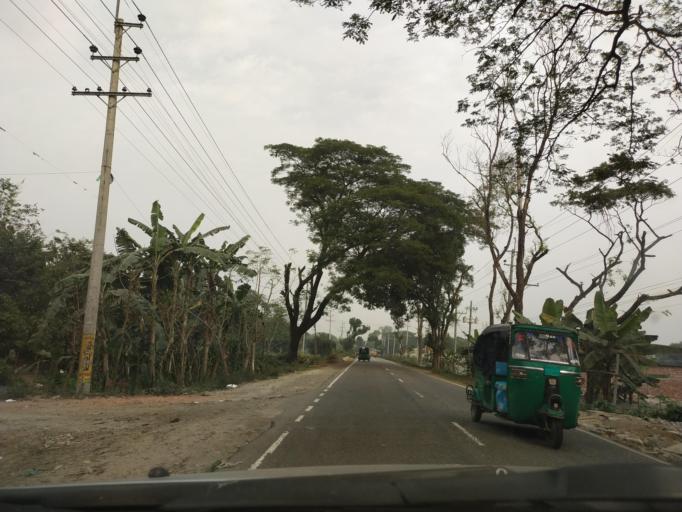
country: BD
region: Dhaka
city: Narsingdi
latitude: 24.0091
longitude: 90.7373
